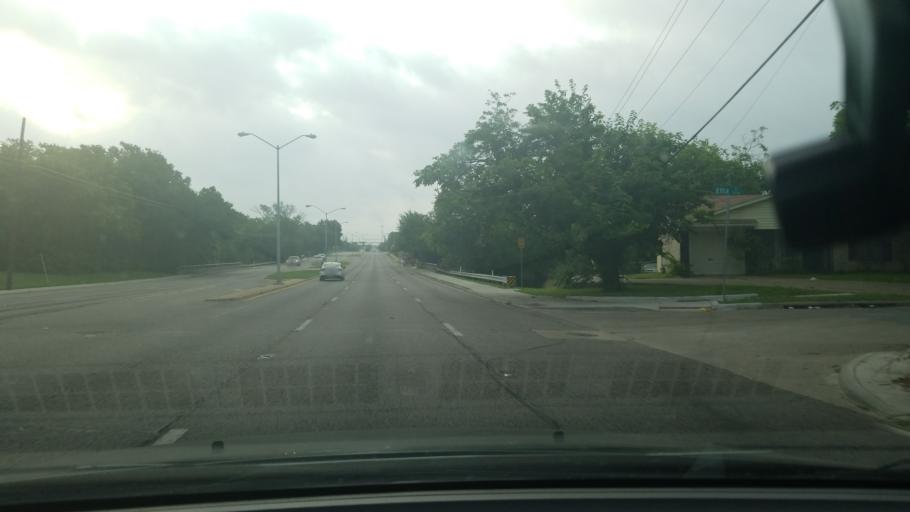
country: US
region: Texas
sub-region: Dallas County
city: Balch Springs
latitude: 32.7634
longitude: -96.6704
